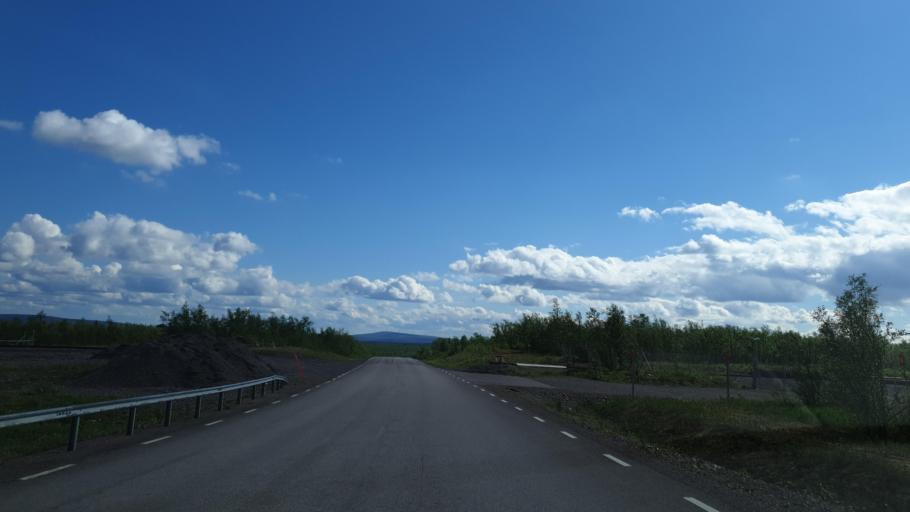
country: SE
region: Norrbotten
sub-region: Kiruna Kommun
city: Kiruna
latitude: 67.7940
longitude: 20.2320
